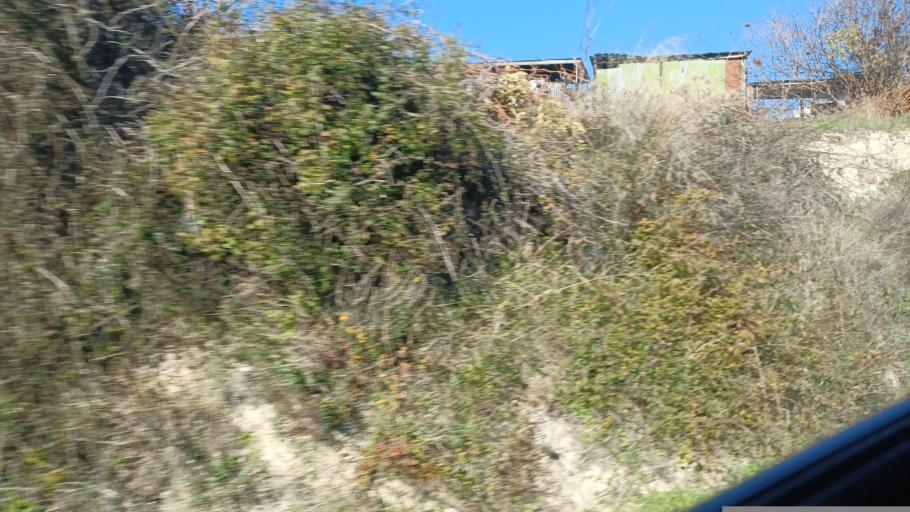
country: CY
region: Limassol
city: Pachna
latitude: 34.8412
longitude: 32.8063
